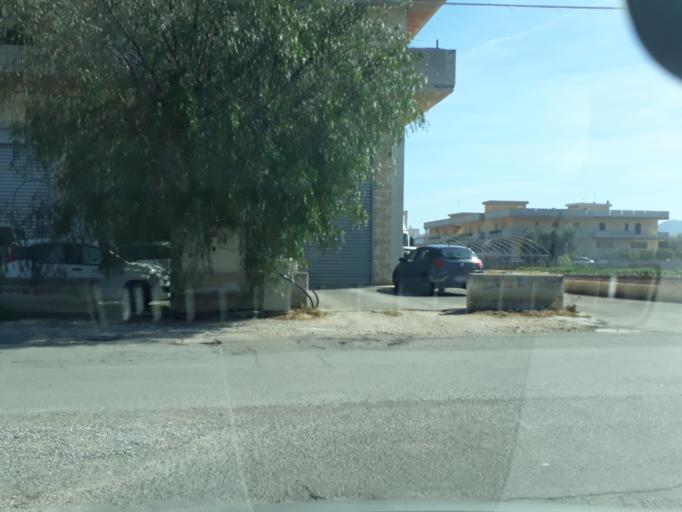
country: IT
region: Apulia
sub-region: Provincia di Brindisi
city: Fasano
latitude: 40.8454
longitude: 17.3522
